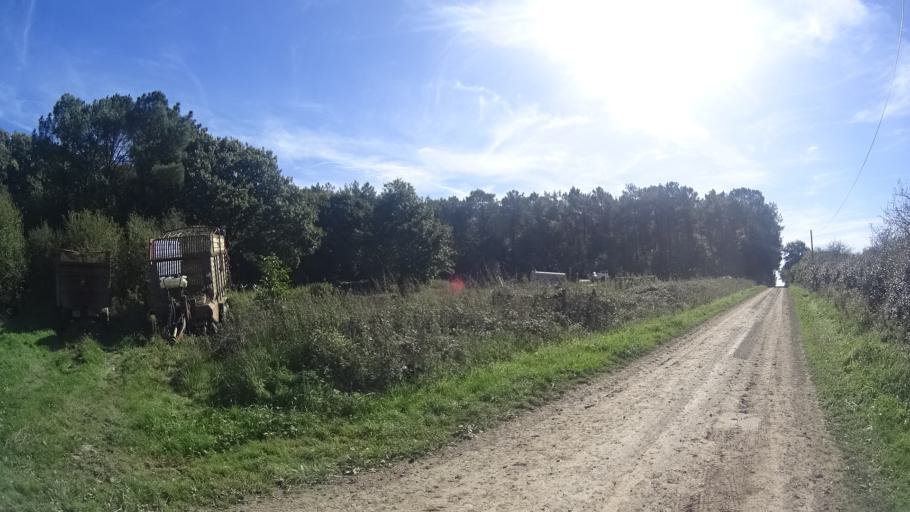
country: FR
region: Brittany
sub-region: Departement du Morbihan
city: La Gacilly
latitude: 47.7494
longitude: -2.1684
